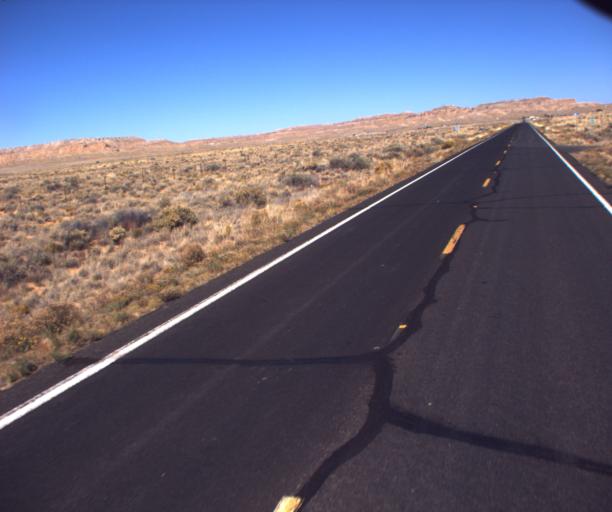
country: US
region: Arizona
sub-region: Navajo County
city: First Mesa
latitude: 35.7641
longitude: -110.5091
